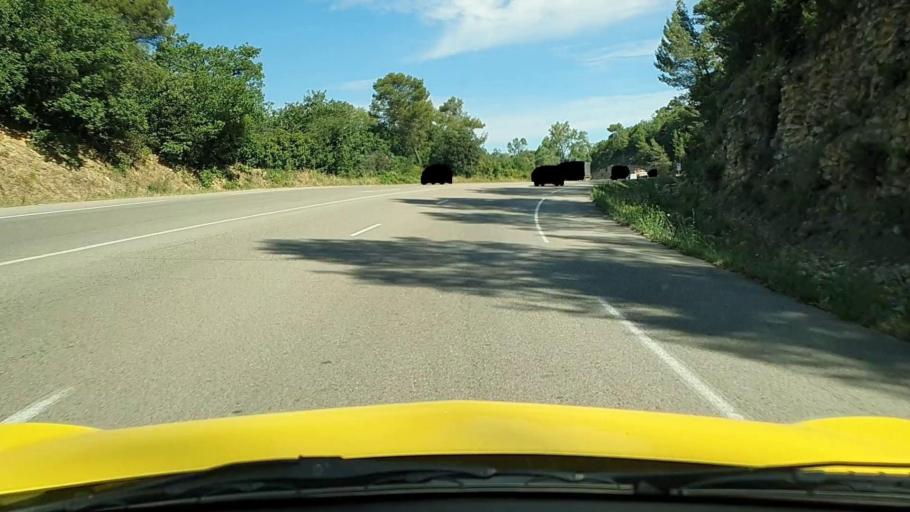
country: FR
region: Languedoc-Roussillon
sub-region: Departement du Gard
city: Saint-Martin-de-Valgalgues
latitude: 44.1513
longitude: 4.0946
